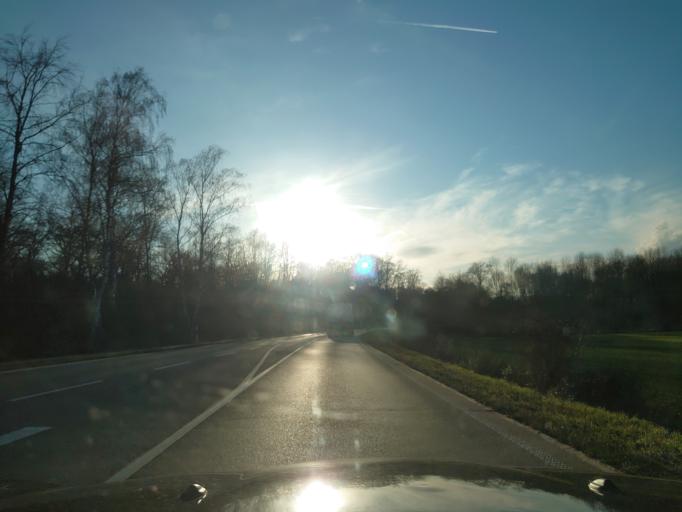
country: DE
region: North Rhine-Westphalia
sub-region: Regierungsbezirk Dusseldorf
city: Dormagen
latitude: 51.0745
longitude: 6.7588
